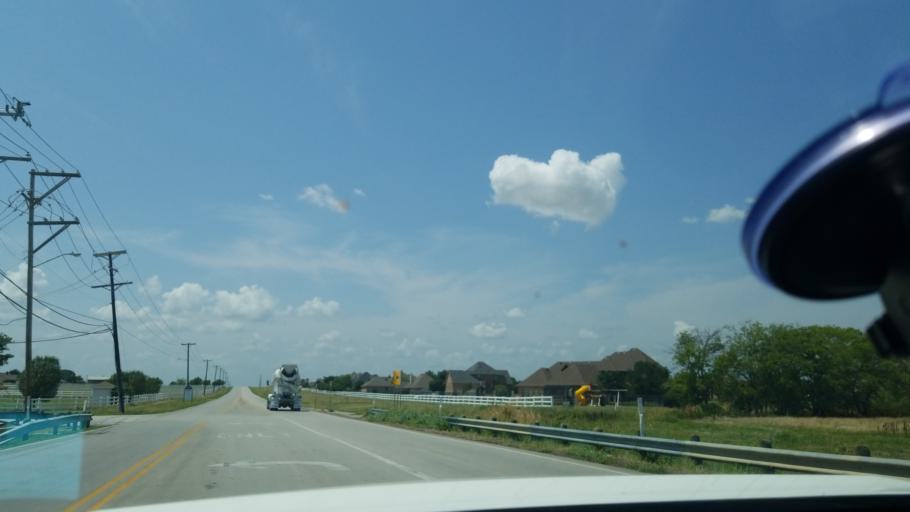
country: US
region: Texas
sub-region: Tarrant County
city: Haslet
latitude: 32.9244
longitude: -97.3743
